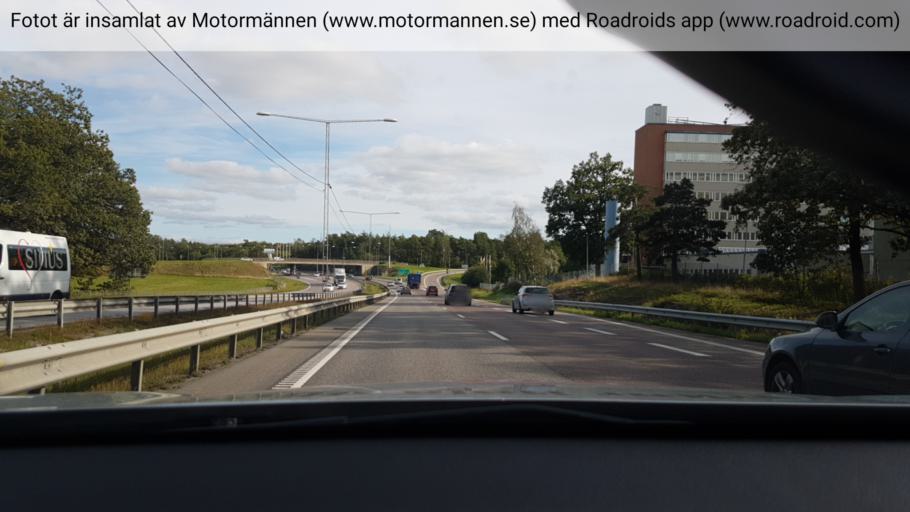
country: SE
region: Stockholm
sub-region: Stockholms Kommun
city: Arsta
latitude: 59.2462
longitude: 18.1052
